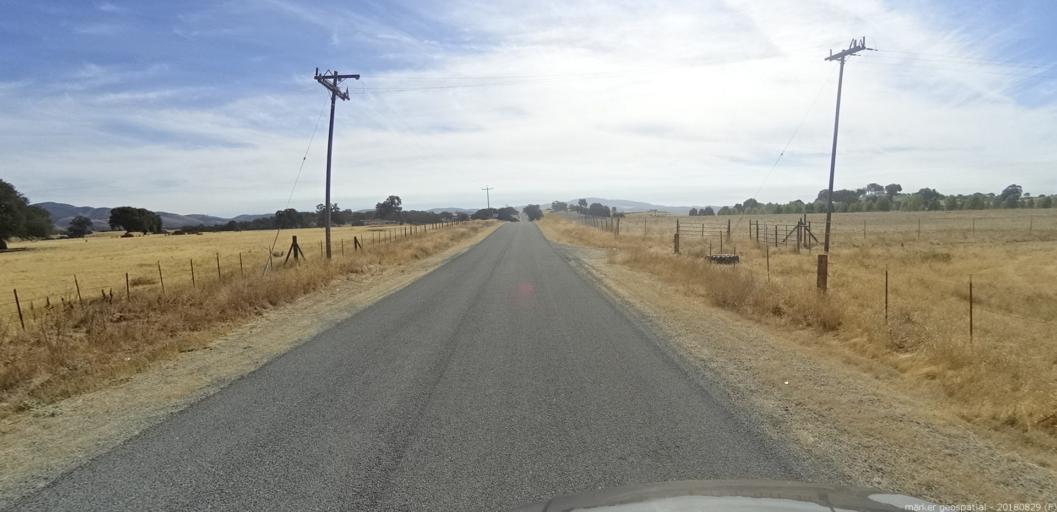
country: US
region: California
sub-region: Monterey County
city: King City
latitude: 35.9663
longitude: -121.1358
